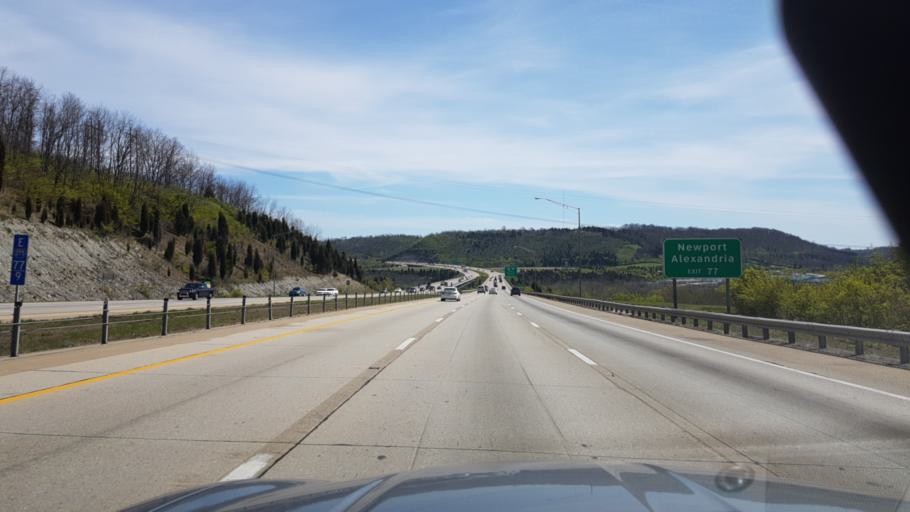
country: US
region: Kentucky
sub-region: Kenton County
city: Taylor Mill
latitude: 39.0227
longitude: -84.4964
